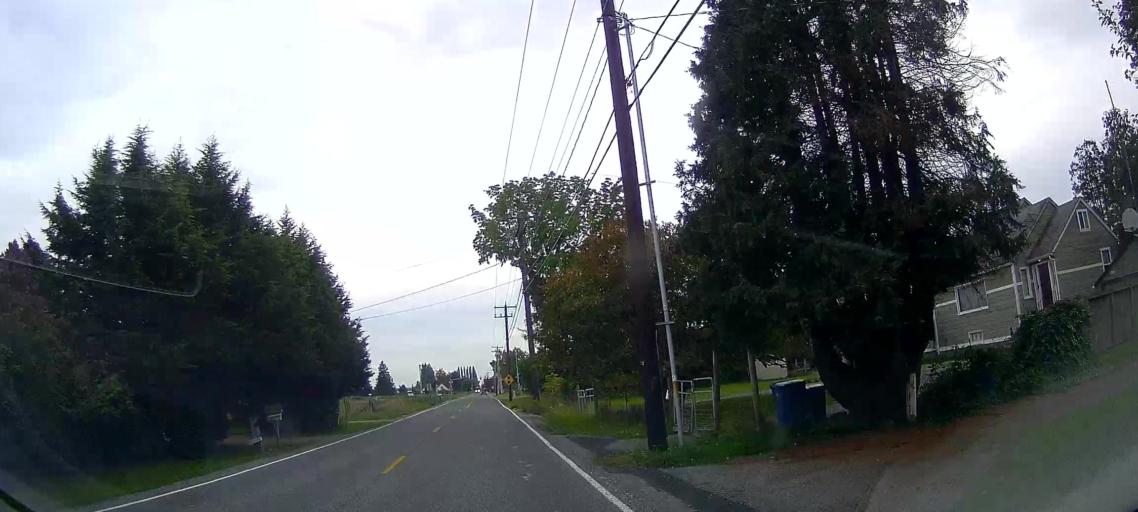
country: US
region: Washington
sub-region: Skagit County
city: Mount Vernon
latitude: 48.4386
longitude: -122.3787
